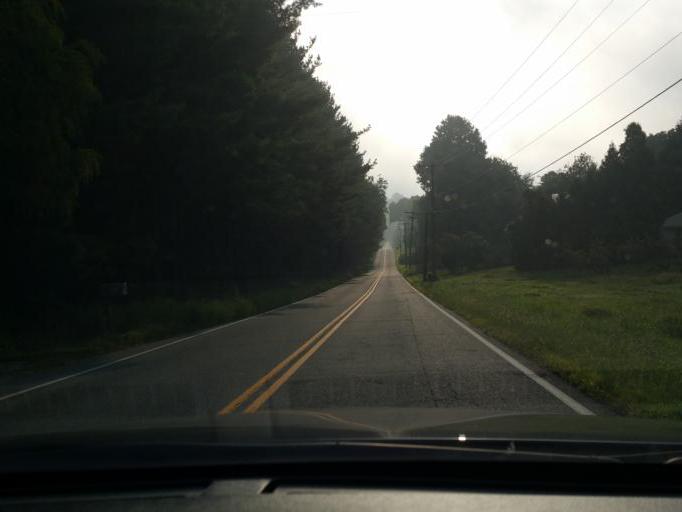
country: US
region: Maryland
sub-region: Cecil County
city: Rising Sun
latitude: 39.6718
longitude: -76.1069
